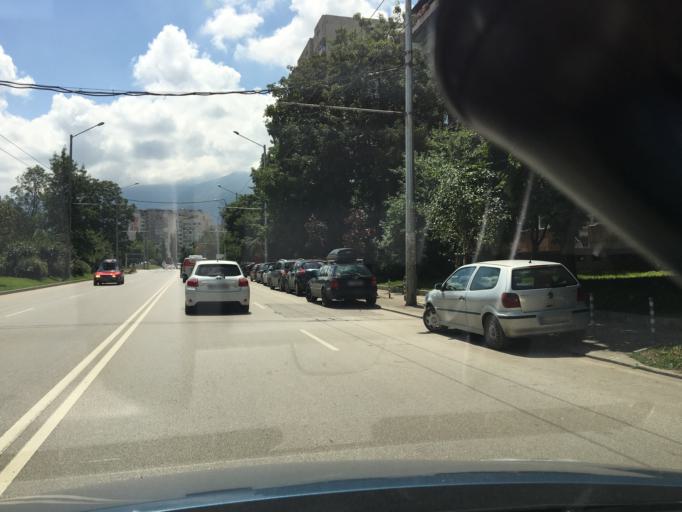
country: BG
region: Sofia-Capital
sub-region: Stolichna Obshtina
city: Sofia
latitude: 42.6672
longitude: 23.3032
